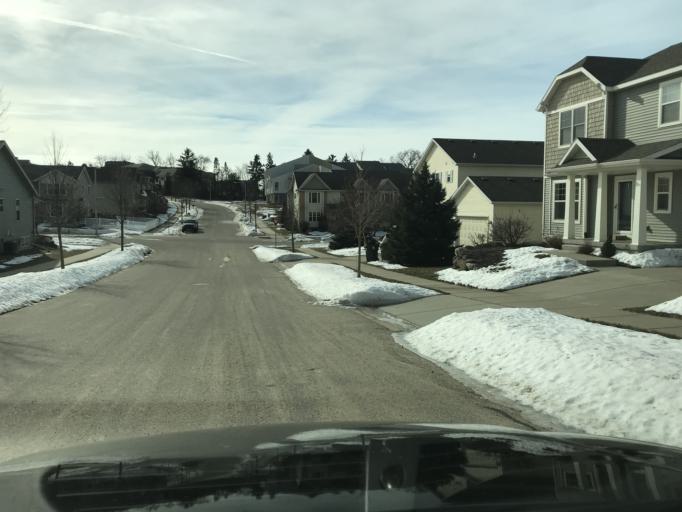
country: US
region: Wisconsin
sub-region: Dane County
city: Monona
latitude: 43.0907
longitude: -89.2810
